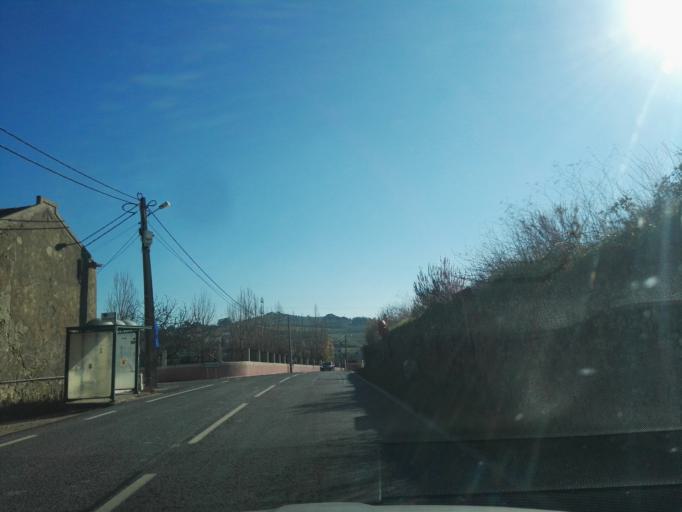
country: PT
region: Lisbon
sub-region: Arruda Dos Vinhos
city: Arruda dos Vinhos
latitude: 38.9777
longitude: -9.0689
